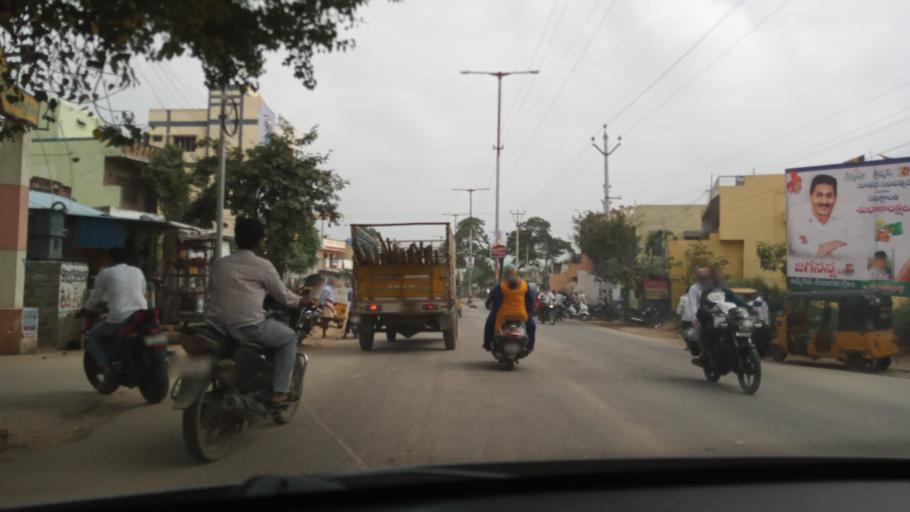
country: IN
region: Andhra Pradesh
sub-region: Chittoor
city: Madanapalle
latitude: 13.5547
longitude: 78.4904
